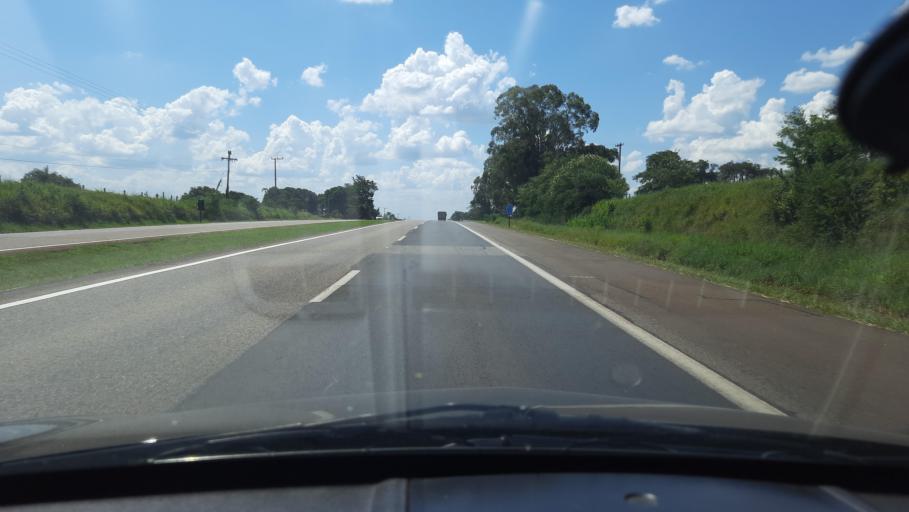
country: BR
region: Sao Paulo
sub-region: Casa Branca
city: Casa Branca
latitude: -21.7240
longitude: -47.0785
